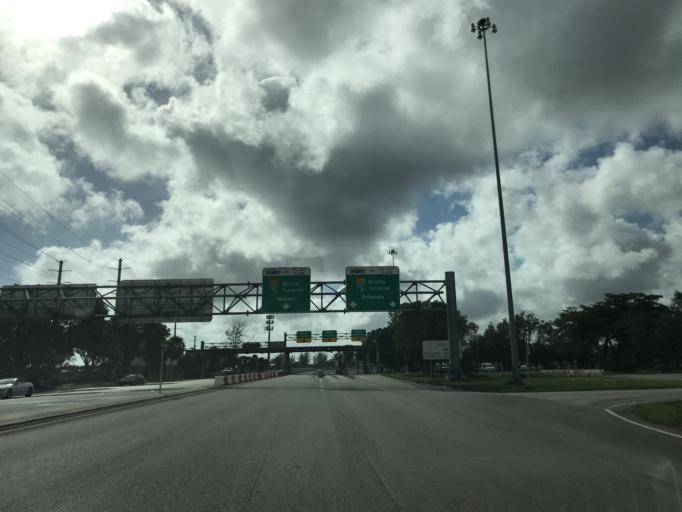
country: US
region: Florida
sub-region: Broward County
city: Coconut Creek
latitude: 26.2736
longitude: -80.1659
